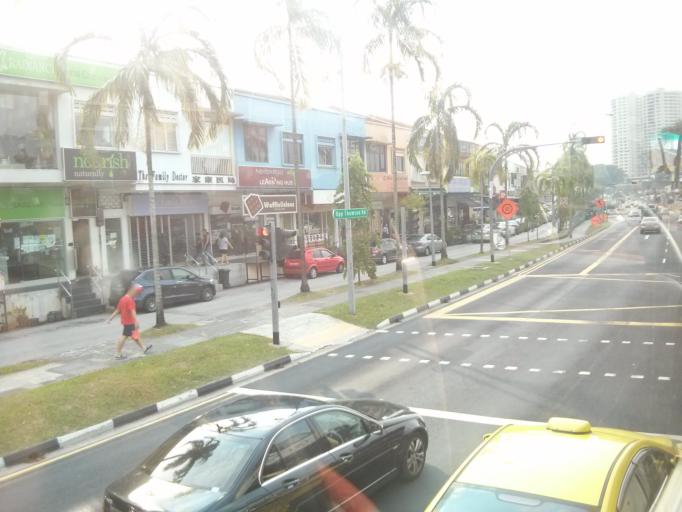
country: SG
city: Singapore
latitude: 1.3523
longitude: 103.8352
